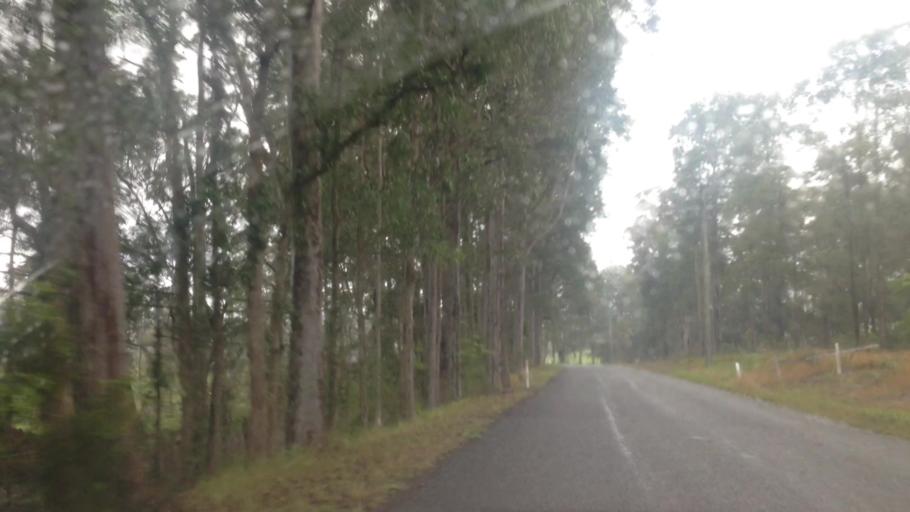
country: AU
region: New South Wales
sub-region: Wyong Shire
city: Little Jilliby
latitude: -33.2128
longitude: 151.3714
